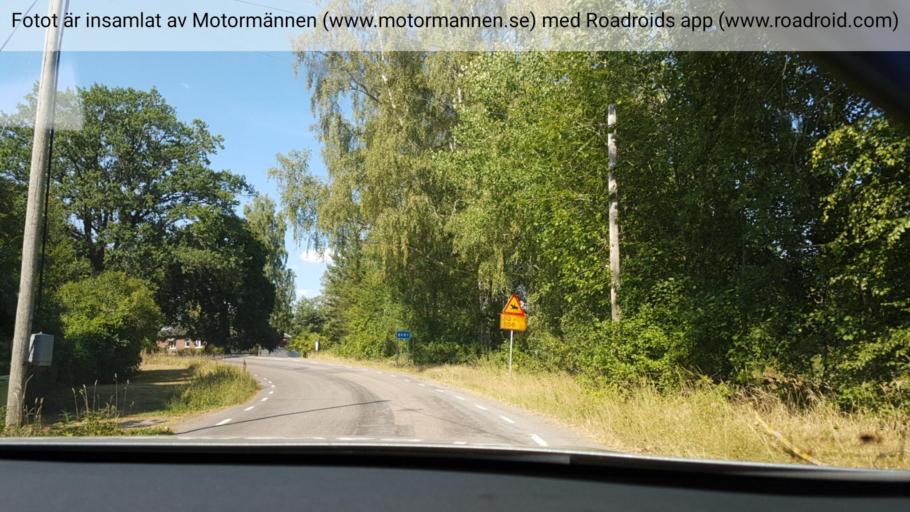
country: SE
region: Vaestra Goetaland
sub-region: Mariestads Kommun
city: Mariestad
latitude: 58.6113
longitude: 13.8785
